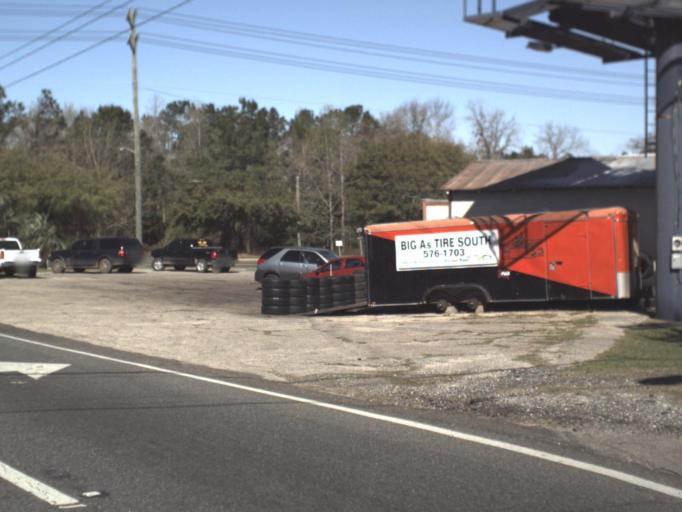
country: US
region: Florida
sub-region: Leon County
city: Tallahassee
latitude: 30.4126
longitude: -84.3026
